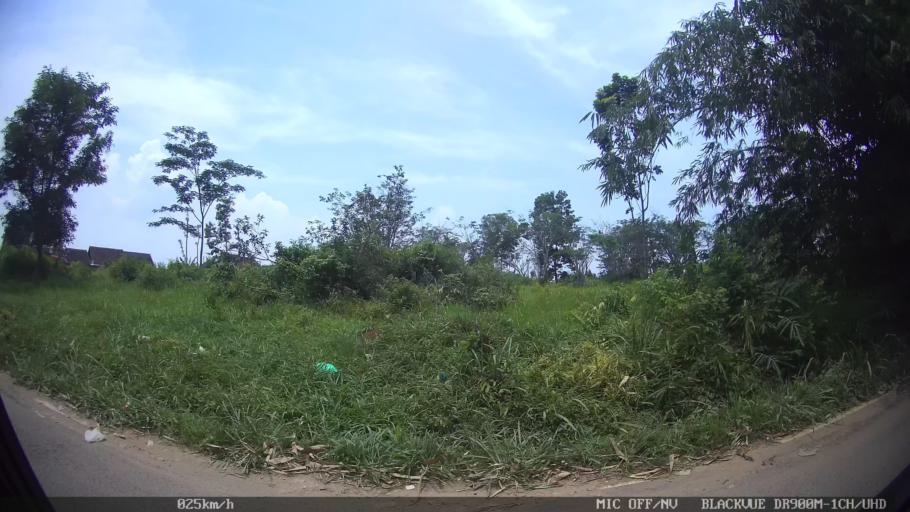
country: ID
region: Lampung
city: Kedaton
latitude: -5.3473
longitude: 105.2426
